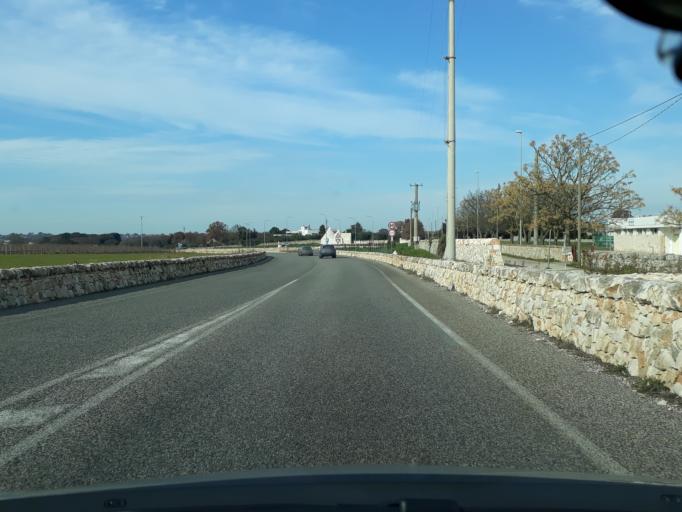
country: IT
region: Apulia
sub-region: Provincia di Bari
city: Locorotondo
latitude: 40.7563
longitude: 17.3432
